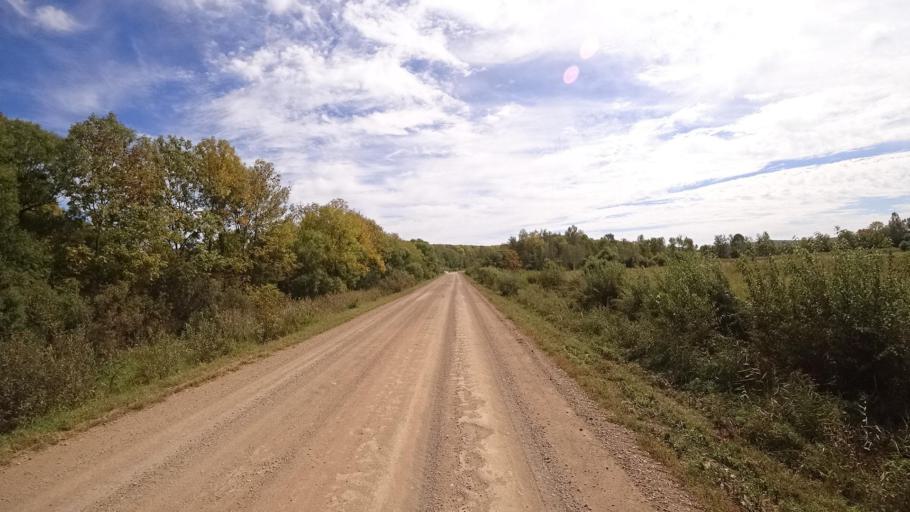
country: RU
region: Primorskiy
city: Yakovlevka
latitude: 44.6363
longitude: 133.5980
